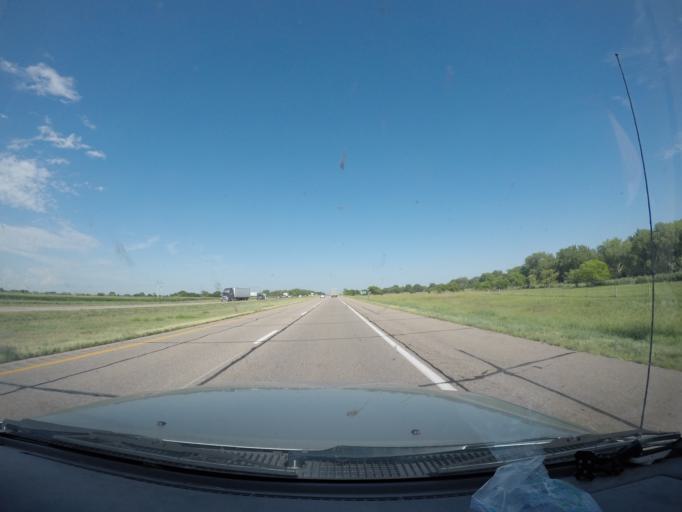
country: US
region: Nebraska
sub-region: Phelps County
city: Holdrege
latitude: 40.6907
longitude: -99.3573
